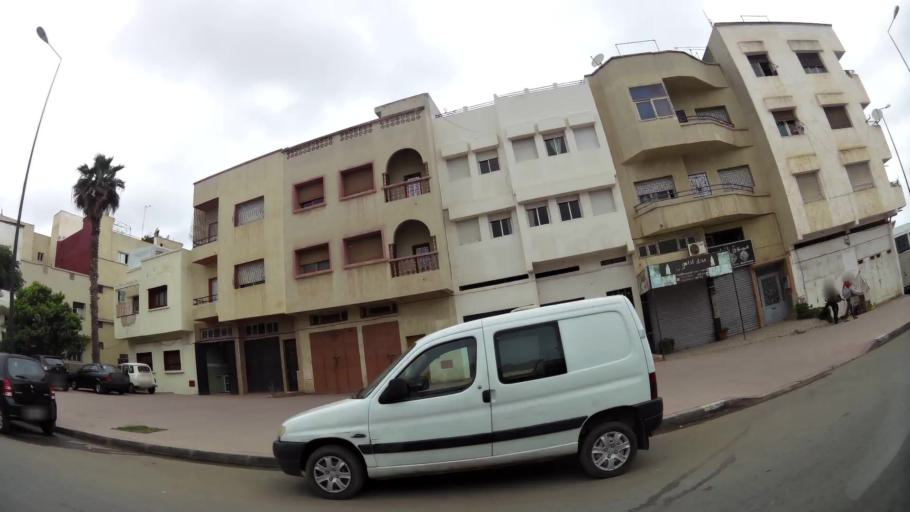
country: MA
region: Rabat-Sale-Zemmour-Zaer
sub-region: Rabat
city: Rabat
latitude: 33.9996
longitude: -6.8146
